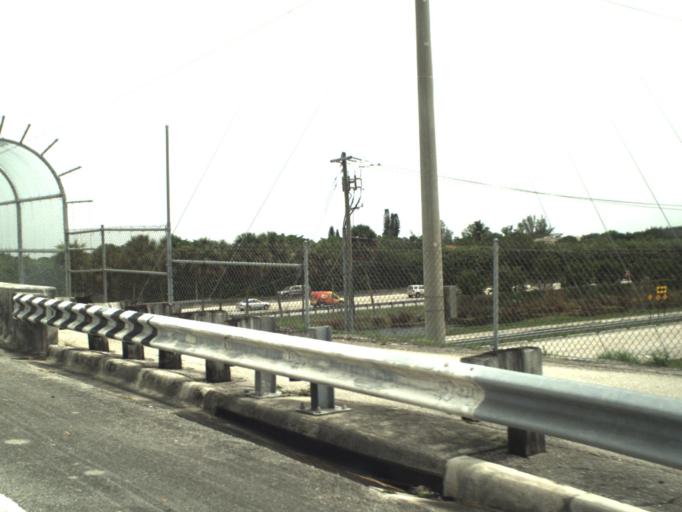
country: US
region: Florida
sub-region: Palm Beach County
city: Boca Pointe
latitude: 26.3501
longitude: -80.1717
